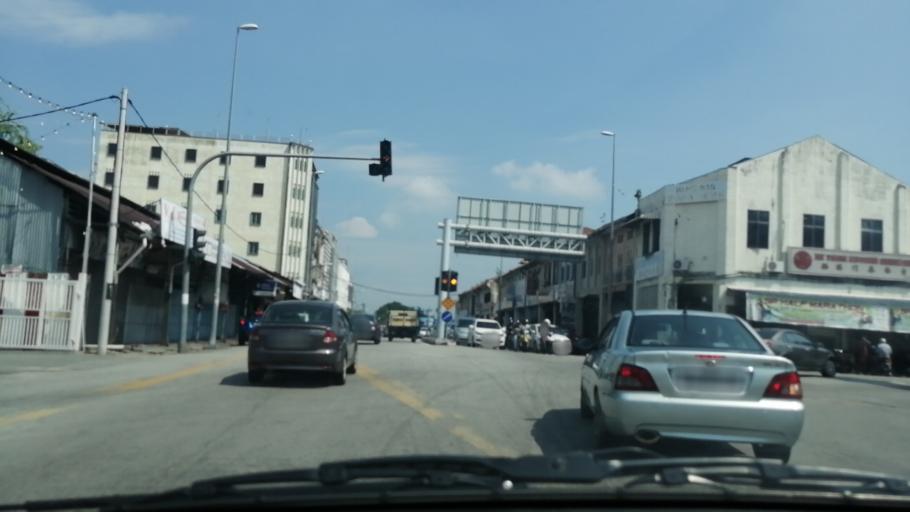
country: MY
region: Kedah
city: Sungai Petani
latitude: 5.6387
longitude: 100.4932
